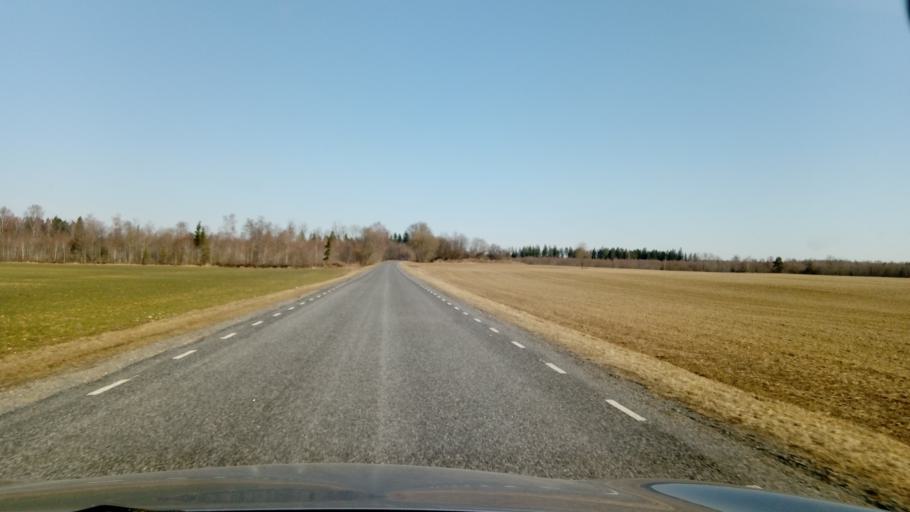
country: EE
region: Laeaene-Virumaa
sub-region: Tamsalu vald
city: Tamsalu
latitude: 59.1807
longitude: 26.1274
